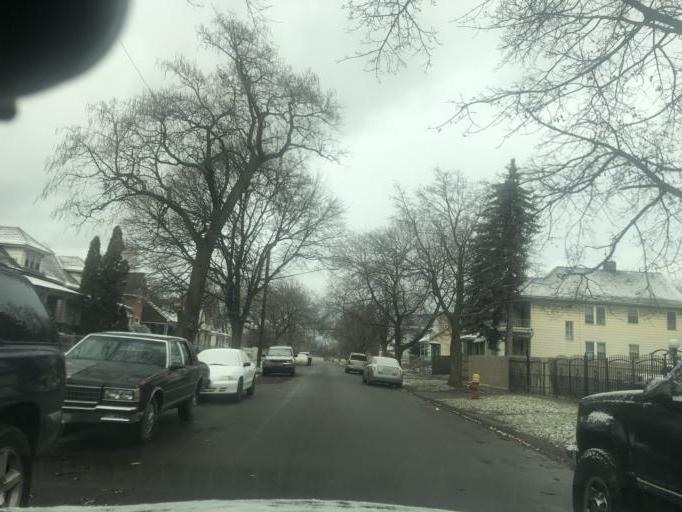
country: US
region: Michigan
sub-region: Wayne County
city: River Rouge
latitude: 42.3112
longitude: -83.1116
